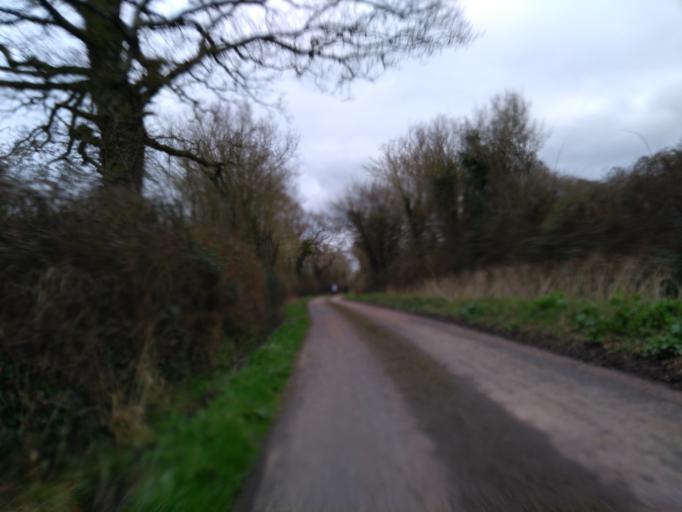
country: GB
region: England
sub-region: Devon
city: Heavitree
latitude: 50.7943
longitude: -3.5009
